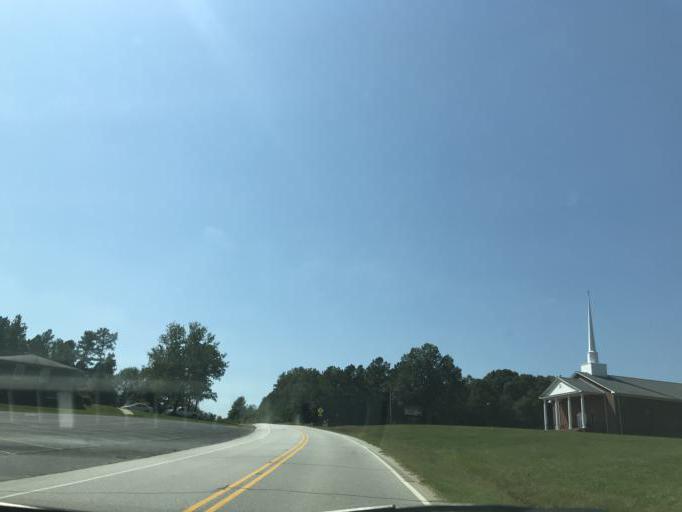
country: US
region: South Carolina
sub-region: Cherokee County
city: Gaffney
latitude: 35.1163
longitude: -81.6948
